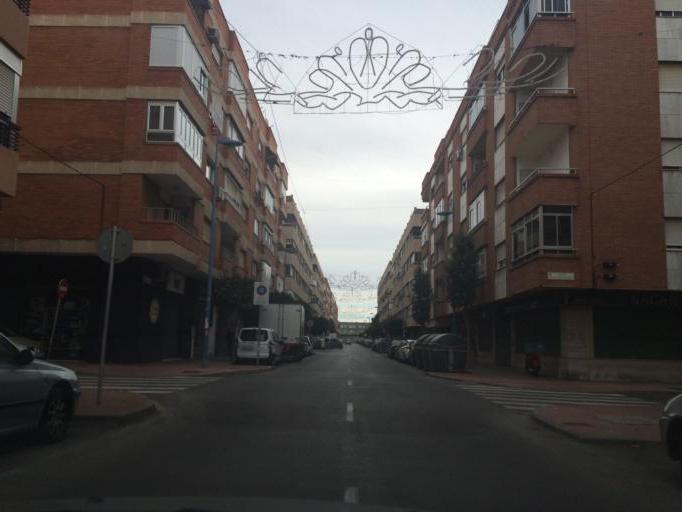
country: ES
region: Andalusia
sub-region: Provincia de Almeria
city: Almeria
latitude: 36.8382
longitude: -2.4511
